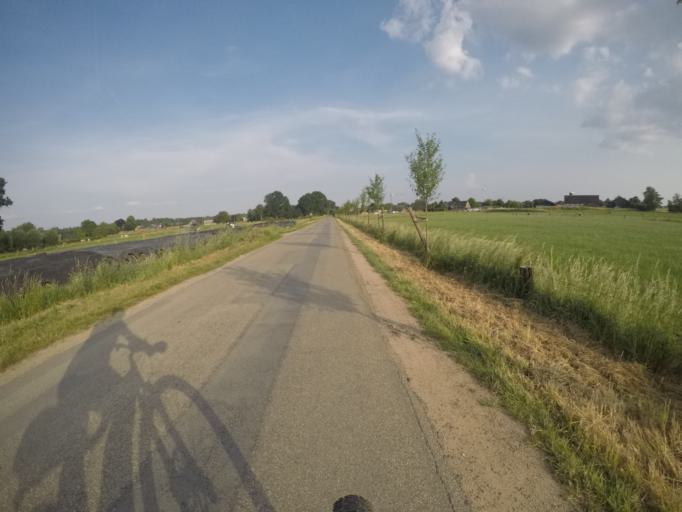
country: DE
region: North Rhine-Westphalia
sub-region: Regierungsbezirk Munster
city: Isselburg
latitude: 51.8316
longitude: 6.4164
